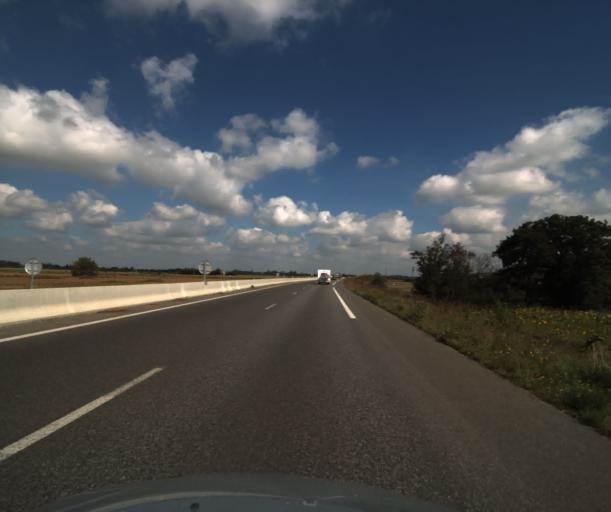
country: FR
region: Midi-Pyrenees
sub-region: Departement de la Haute-Garonne
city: Vernet
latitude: 43.4324
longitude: 1.4172
